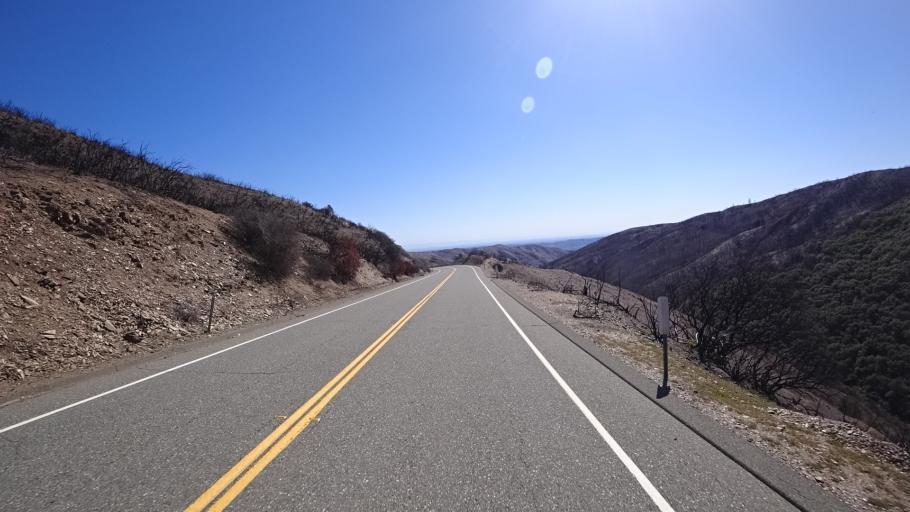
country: US
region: California
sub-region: Tehama County
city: Rancho Tehama Reserve
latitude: 39.6613
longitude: -122.6526
